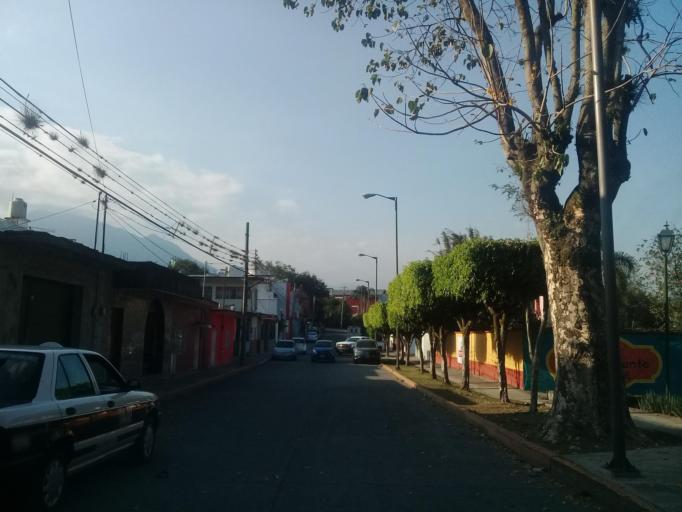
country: MX
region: Veracruz
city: Orizaba
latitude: 18.8540
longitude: -97.1133
